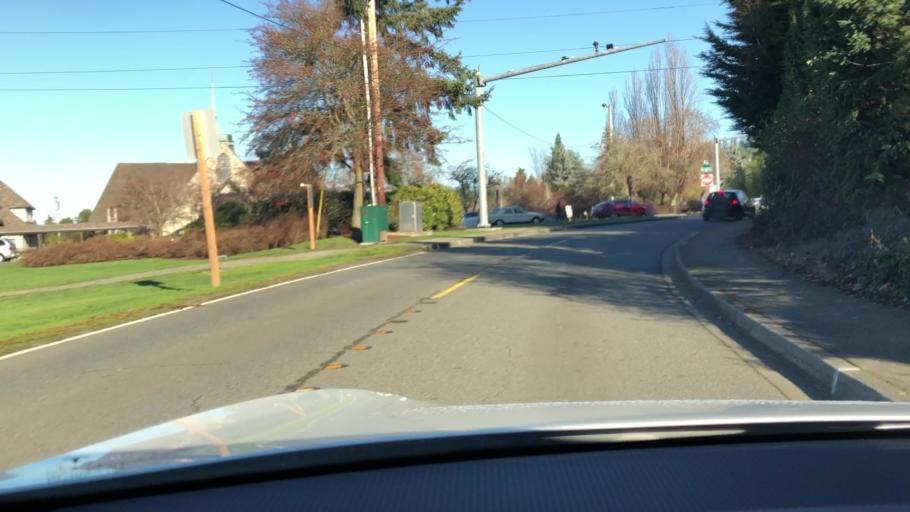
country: US
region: Washington
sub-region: King County
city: Medina
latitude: 47.6205
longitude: -122.2288
